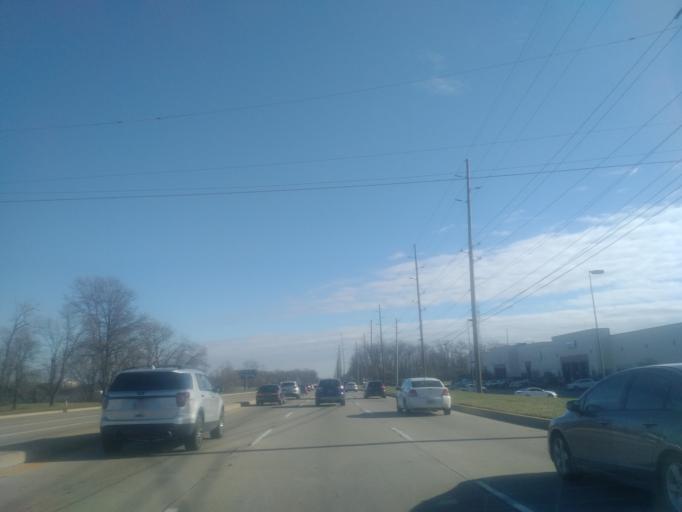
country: US
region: Indiana
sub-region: Boone County
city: Zionsville
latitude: 39.9114
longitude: -86.2403
